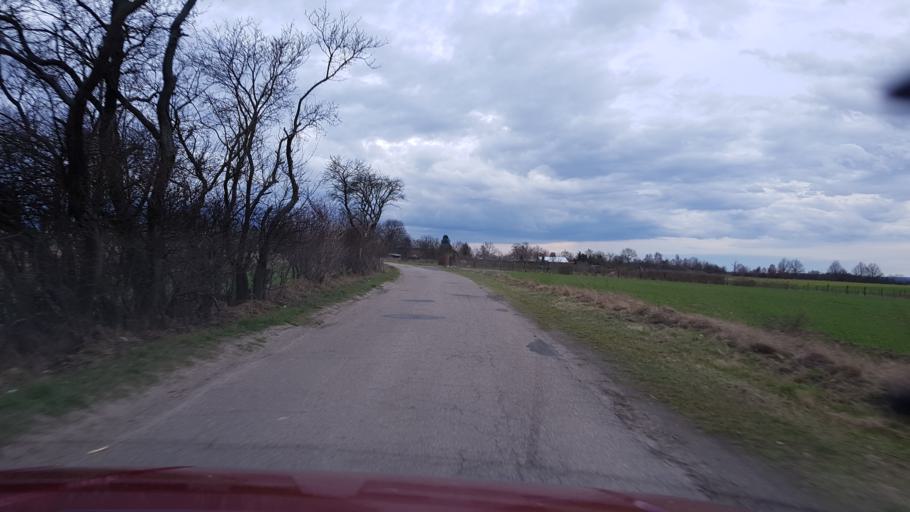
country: PL
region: West Pomeranian Voivodeship
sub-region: Powiat gryfinski
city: Stare Czarnowo
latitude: 53.3285
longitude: 14.6759
